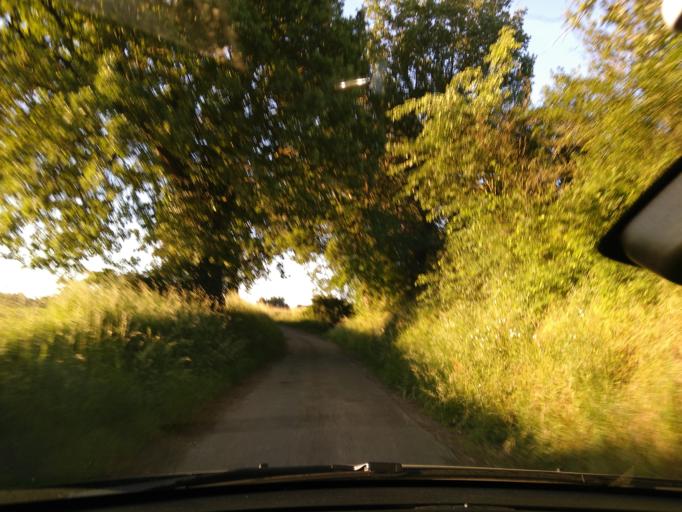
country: FR
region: Midi-Pyrenees
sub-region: Departement de la Haute-Garonne
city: Grenade
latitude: 43.7529
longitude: 1.3001
